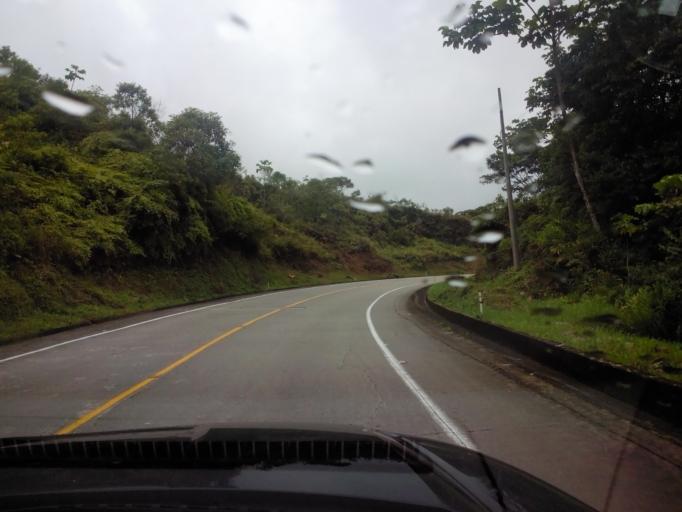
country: EC
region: Napo
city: Archidona
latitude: -0.7853
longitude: -77.7806
